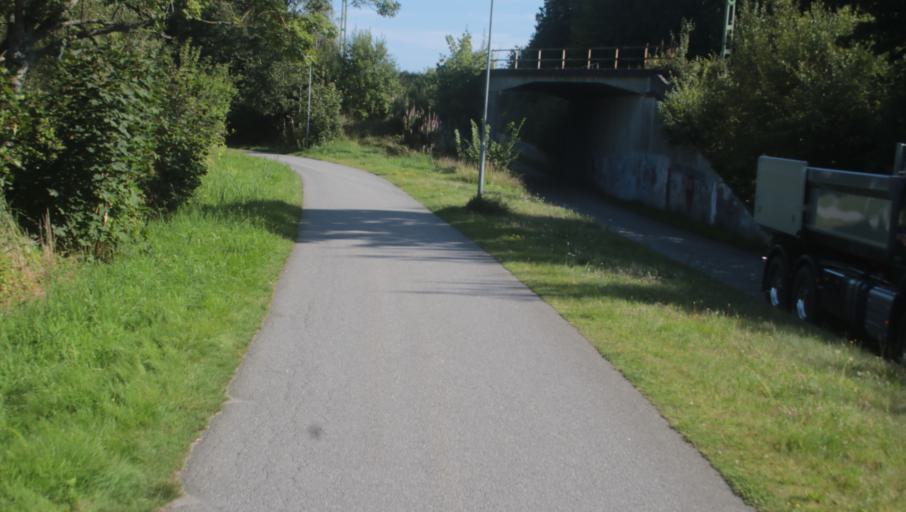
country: SE
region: Blekinge
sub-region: Karlshamns Kommun
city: Karlshamn
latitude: 56.1792
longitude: 14.8496
